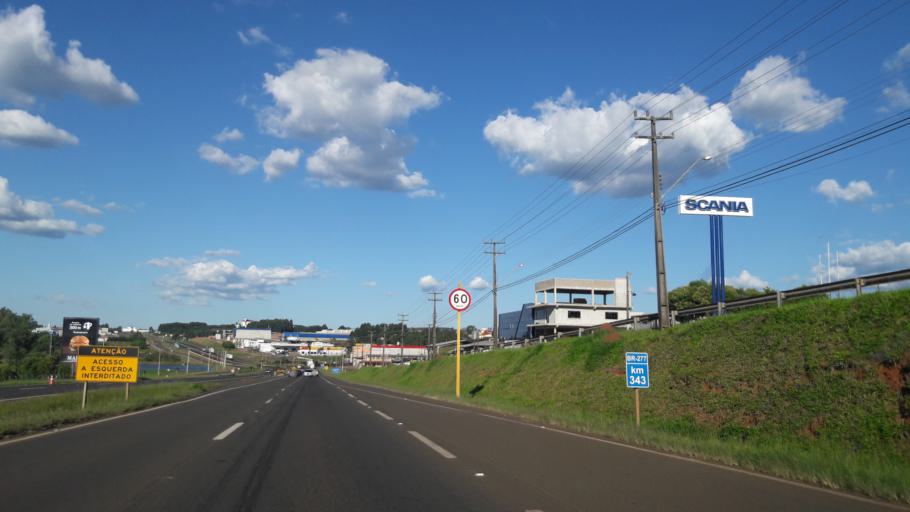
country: BR
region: Parana
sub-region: Guarapuava
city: Guarapuava
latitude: -25.3600
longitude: -51.4674
